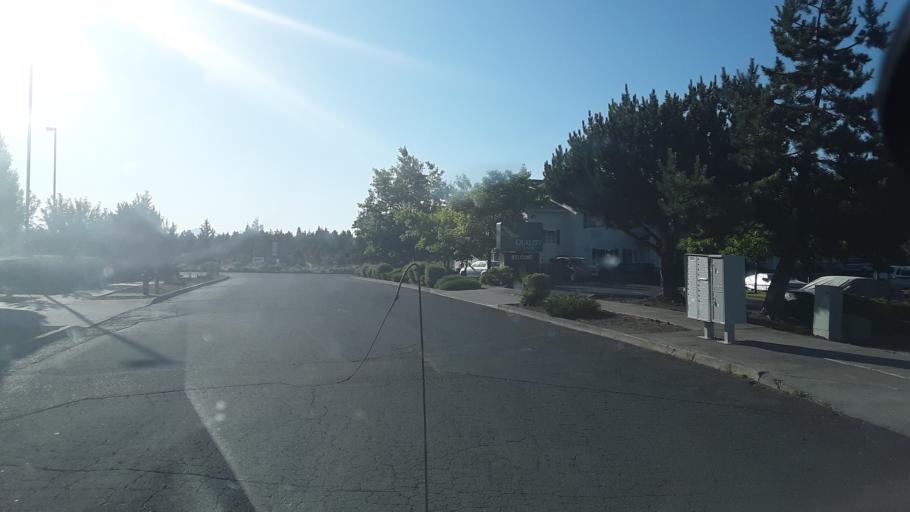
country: US
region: Oregon
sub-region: Deschutes County
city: Bend
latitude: 44.1149
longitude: -121.2926
